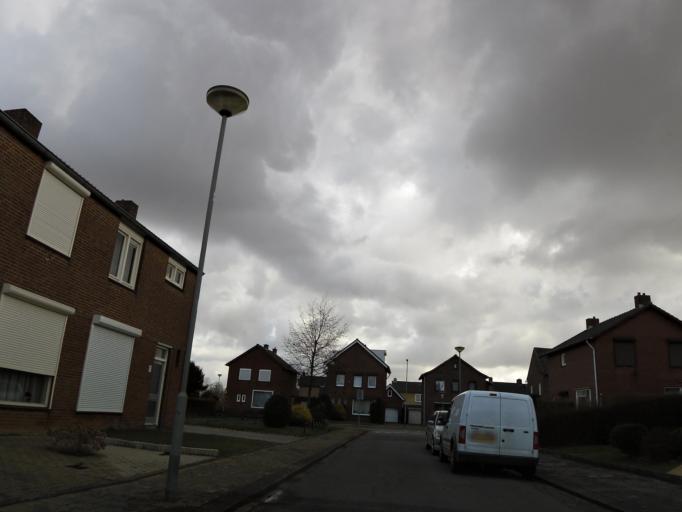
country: NL
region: Limburg
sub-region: Gemeente Stein
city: Berg
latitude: 51.0069
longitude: 5.7716
